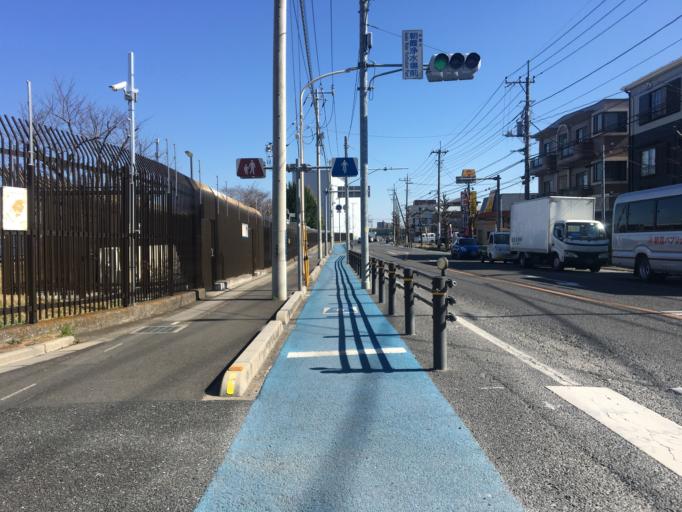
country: JP
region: Saitama
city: Shiki
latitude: 35.8206
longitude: 139.5899
